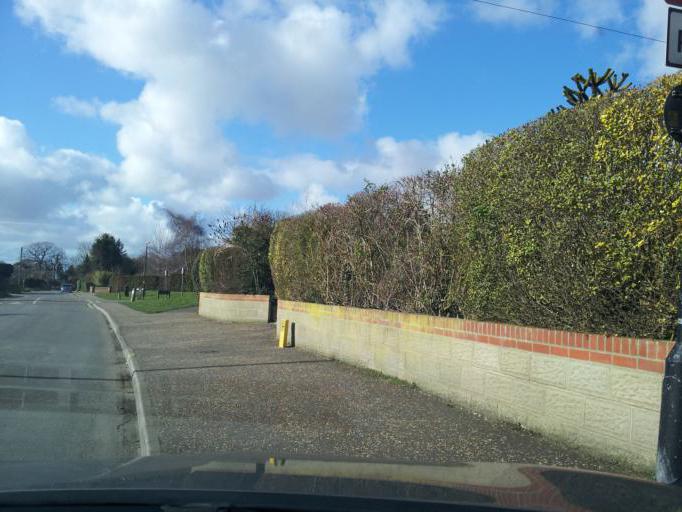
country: GB
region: England
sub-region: Norfolk
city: Mattishall
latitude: 52.6591
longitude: 1.0318
